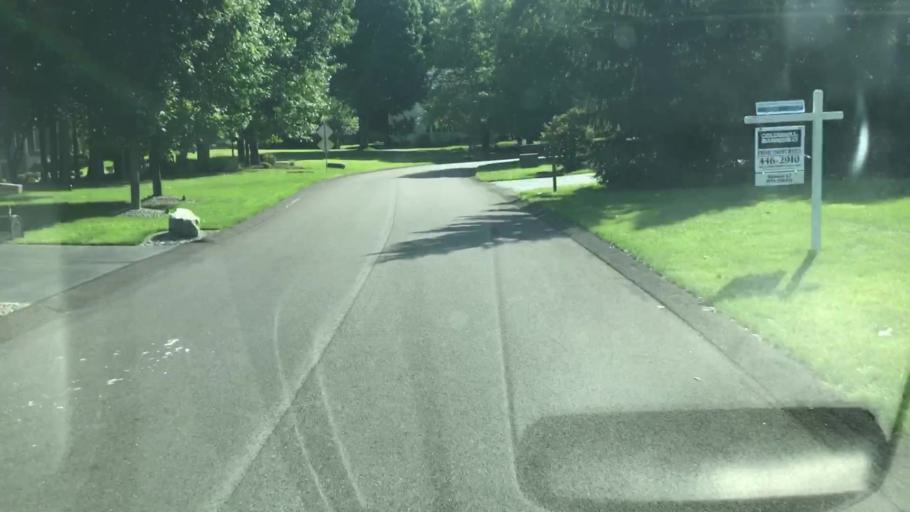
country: US
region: New York
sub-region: Onondaga County
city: Manlius
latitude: 42.9904
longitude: -75.9791
